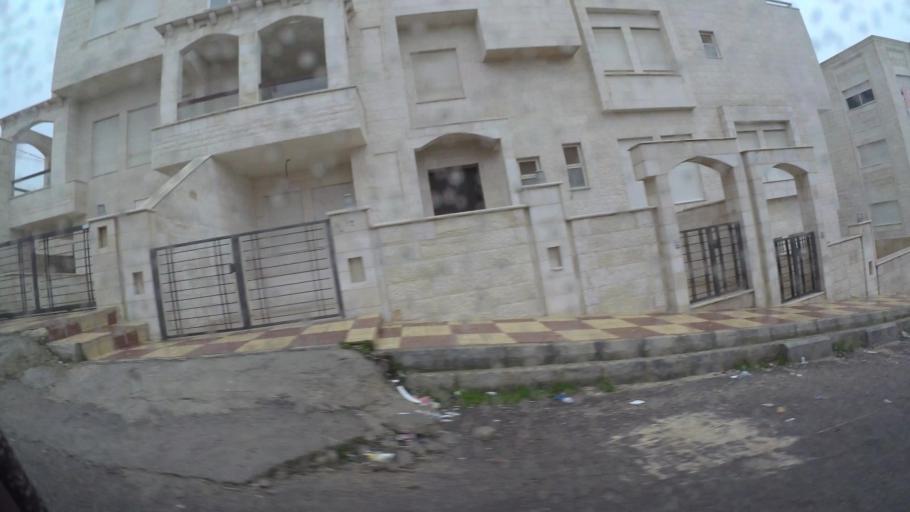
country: JO
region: Amman
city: Al Jubayhah
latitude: 32.0333
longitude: 35.8501
